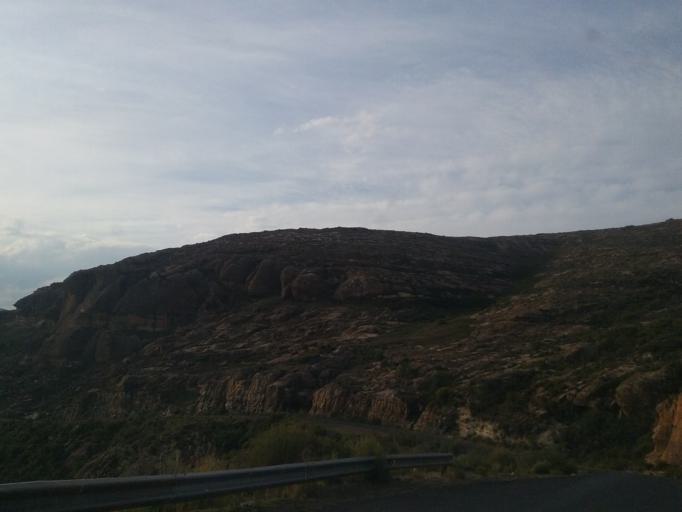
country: LS
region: Quthing
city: Quthing
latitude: -30.2205
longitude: 27.9117
